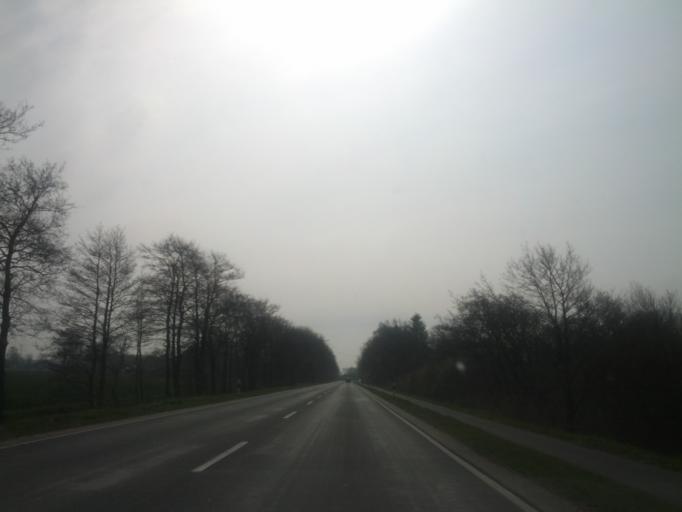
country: DE
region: Lower Saxony
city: Osteel
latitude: 53.5607
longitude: 7.2494
